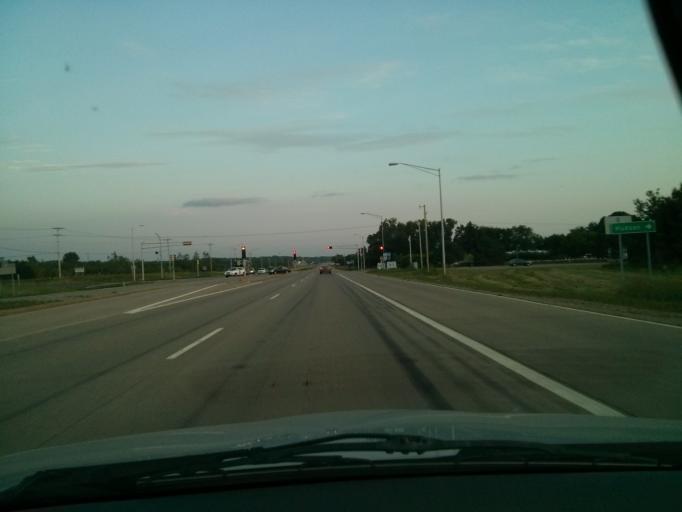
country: US
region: Wisconsin
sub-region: Saint Croix County
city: Hudson
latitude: 44.9792
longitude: -92.6802
